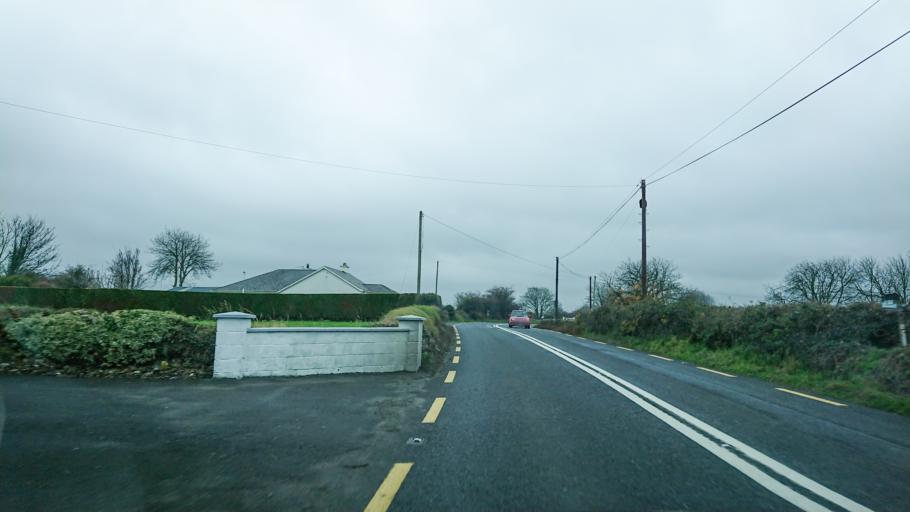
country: IE
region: Leinster
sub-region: Kilkenny
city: Mooncoin
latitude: 52.3035
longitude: -7.2755
